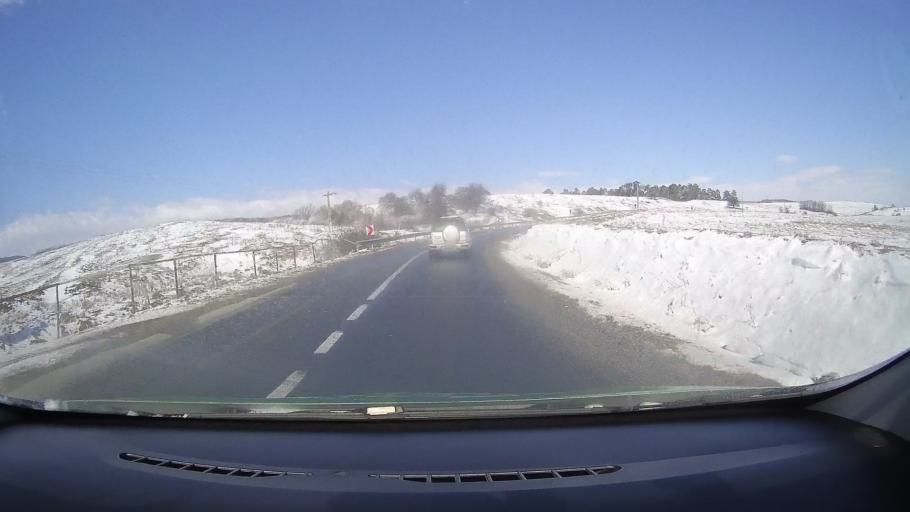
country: RO
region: Sibiu
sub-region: Comuna Rosia
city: Rosia
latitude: 45.8109
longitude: 24.3606
